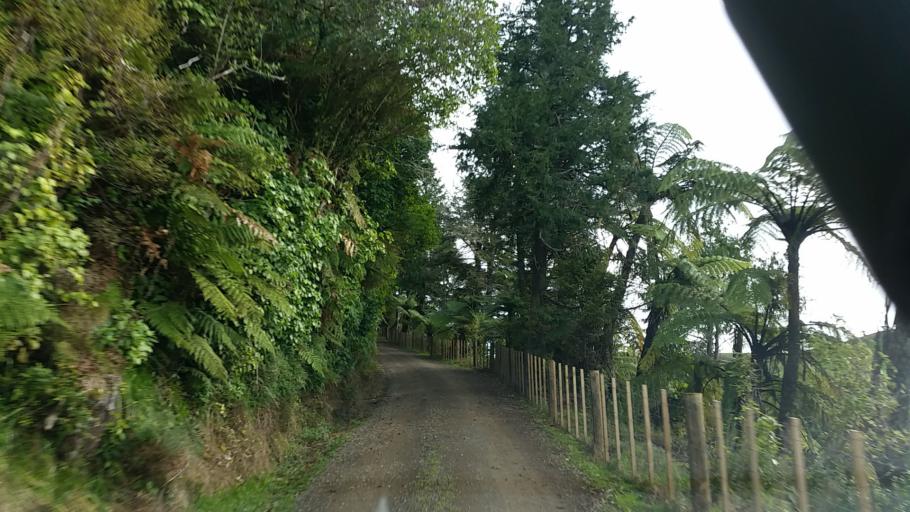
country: NZ
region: Taranaki
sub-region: New Plymouth District
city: Waitara
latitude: -39.0497
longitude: 174.3994
